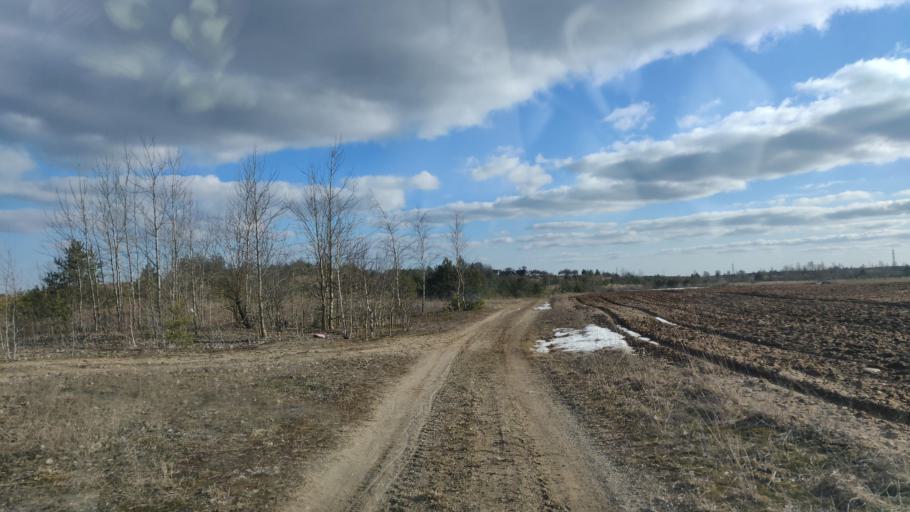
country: LT
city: Lentvaris
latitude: 54.6171
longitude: 24.9974
